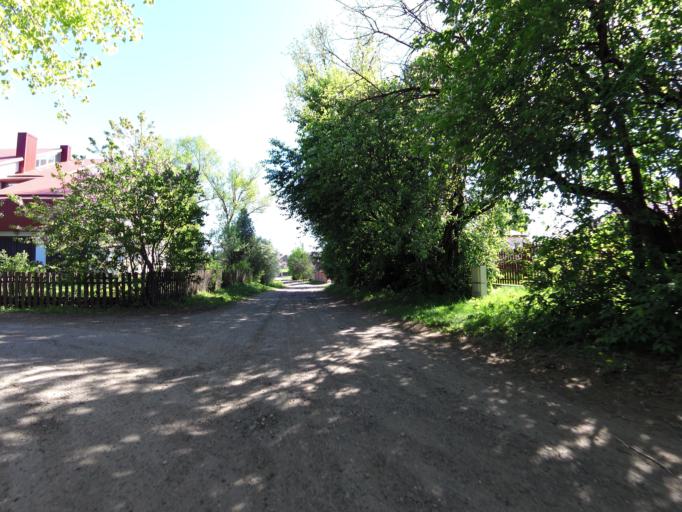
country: LT
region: Vilnius County
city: Pilaite
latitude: 54.6981
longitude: 25.1639
